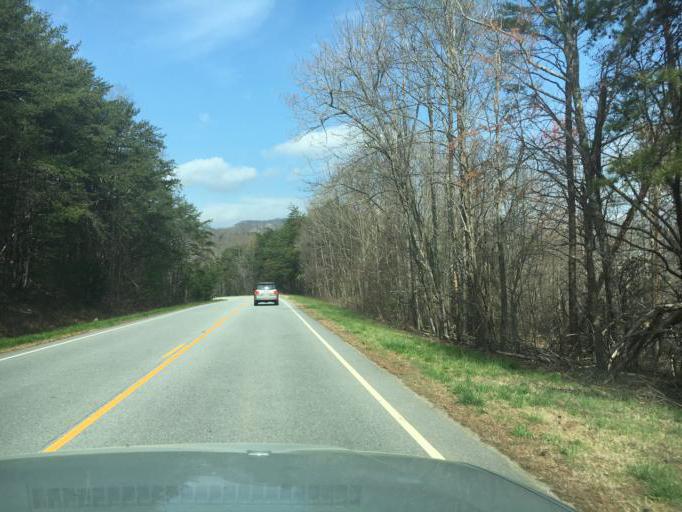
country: US
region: South Carolina
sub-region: Greenville County
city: Tigerville
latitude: 35.1258
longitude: -82.2901
